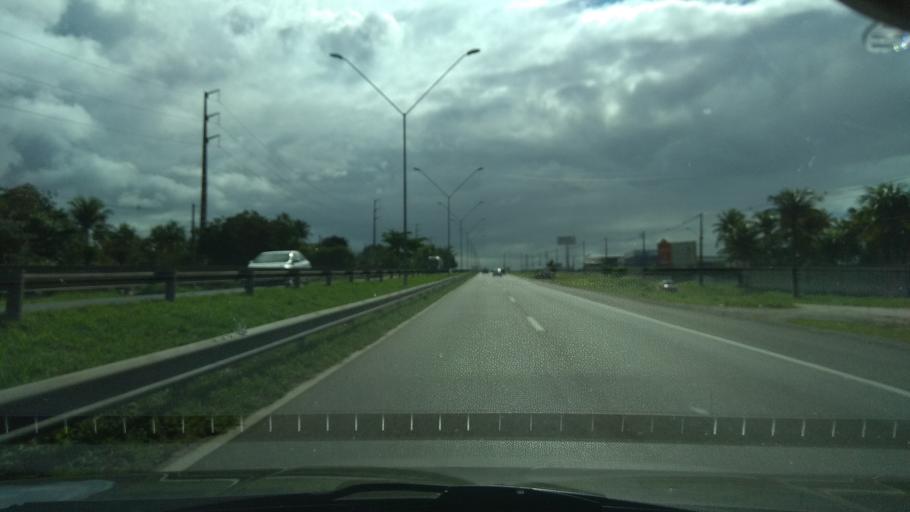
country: BR
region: Bahia
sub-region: Conceicao Do Jacuipe
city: Conceicao do Jacuipe
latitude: -12.3229
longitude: -38.8684
